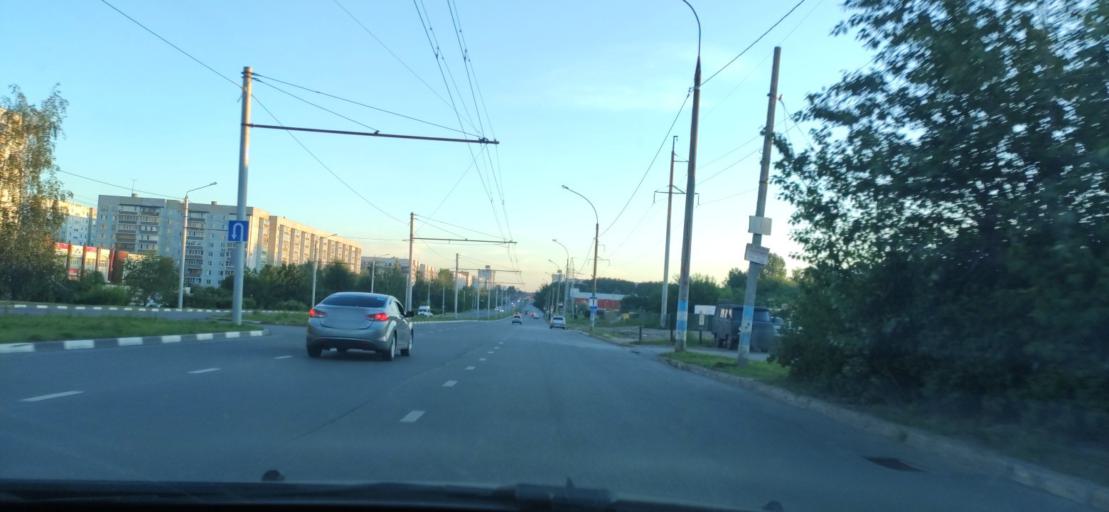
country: RU
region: Ulyanovsk
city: Mirnyy
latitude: 54.3869
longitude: 48.6075
